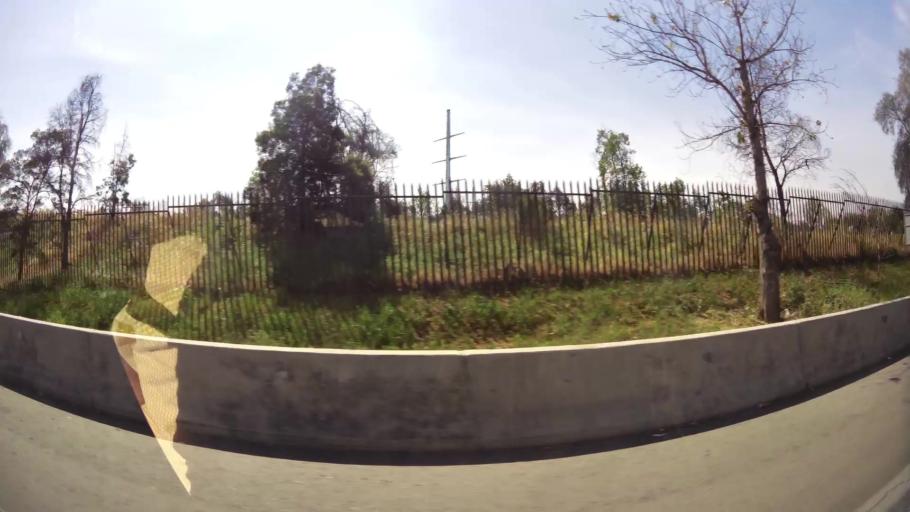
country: CL
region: Santiago Metropolitan
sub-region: Provincia de Santiago
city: Lo Prado
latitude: -33.4562
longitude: -70.7244
